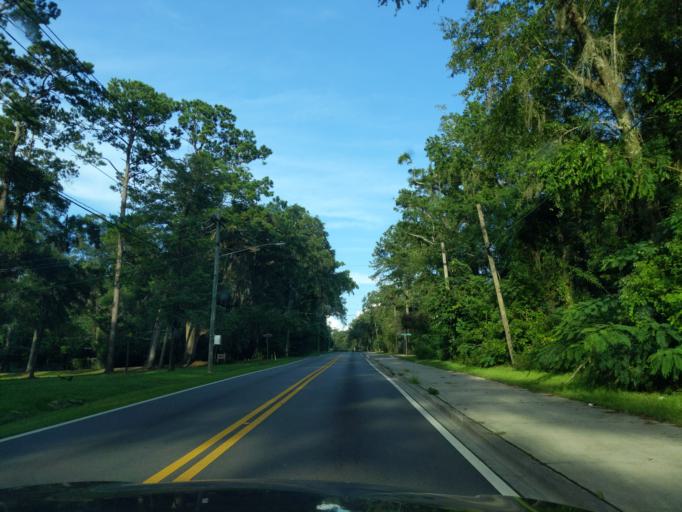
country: US
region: Florida
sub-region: Leon County
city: Tallahassee
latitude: 30.4200
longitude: -84.2697
